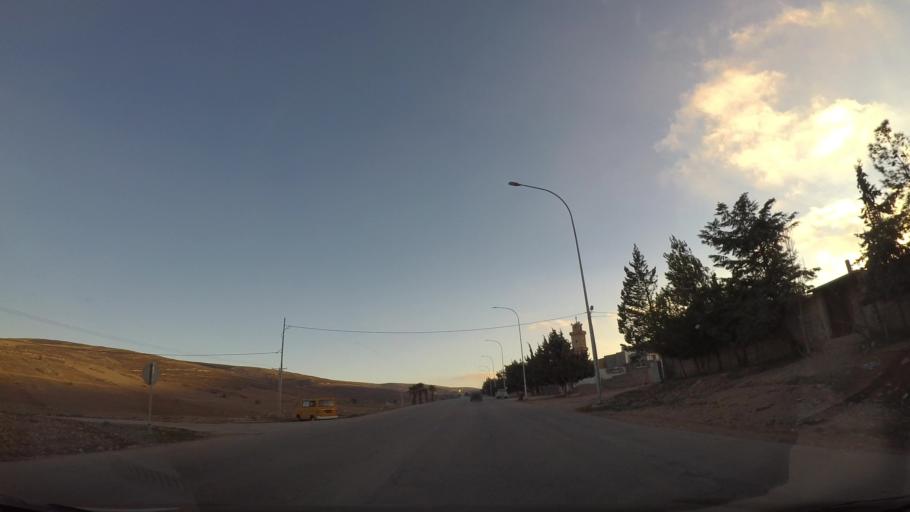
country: JO
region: Ma'an
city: Petra
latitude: 30.4325
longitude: 35.5161
